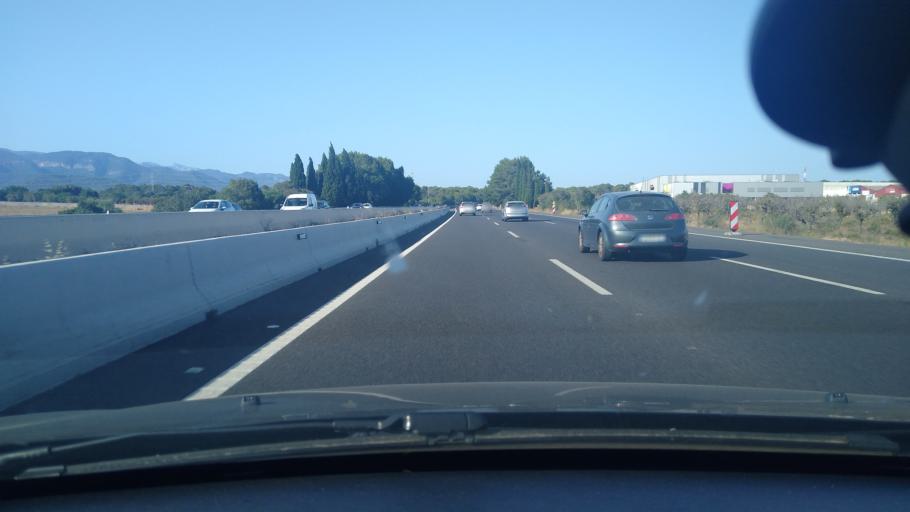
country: ES
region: Balearic Islands
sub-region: Illes Balears
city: Marratxi
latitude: 39.6294
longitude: 2.7232
